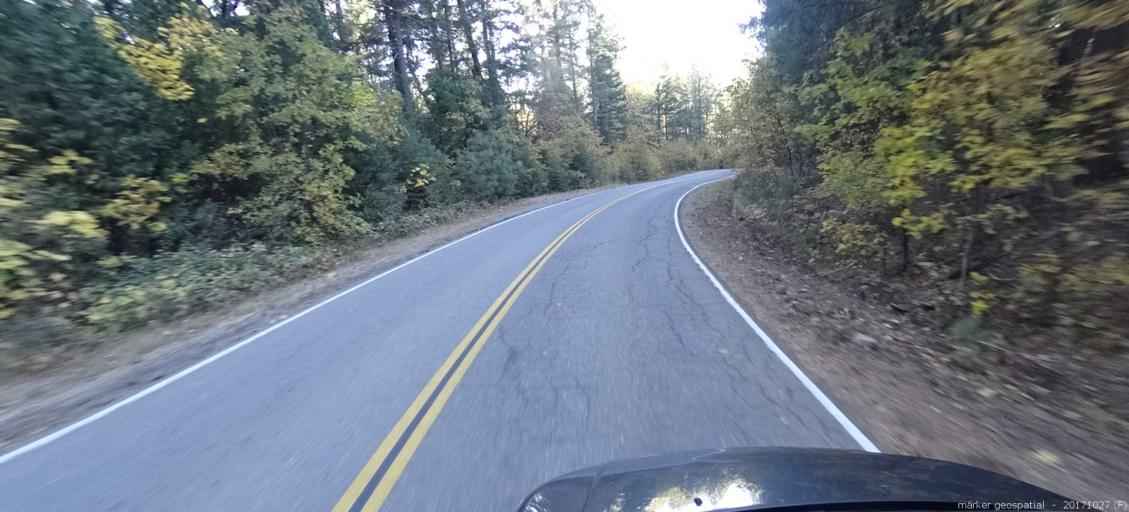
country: US
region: California
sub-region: Shasta County
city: Burney
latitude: 40.9926
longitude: -121.9205
